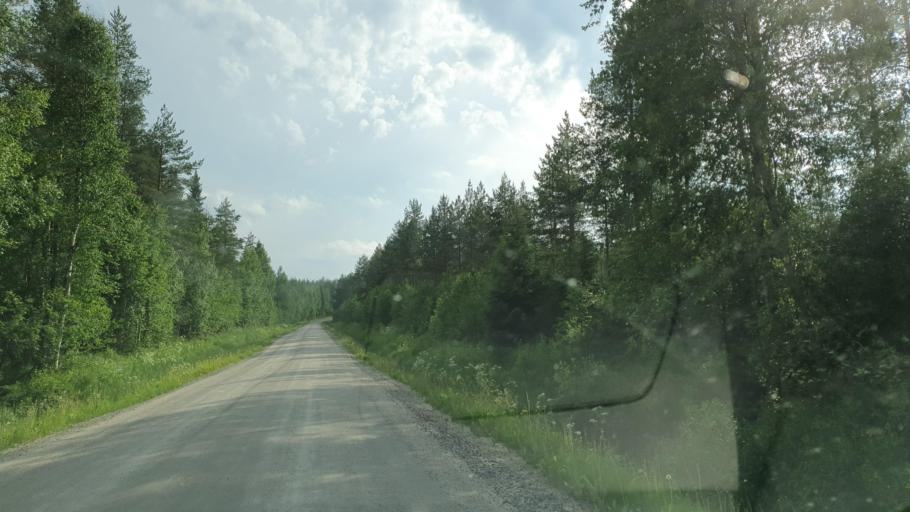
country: FI
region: Kainuu
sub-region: Kehys-Kainuu
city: Kuhmo
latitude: 64.0939
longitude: 29.6053
